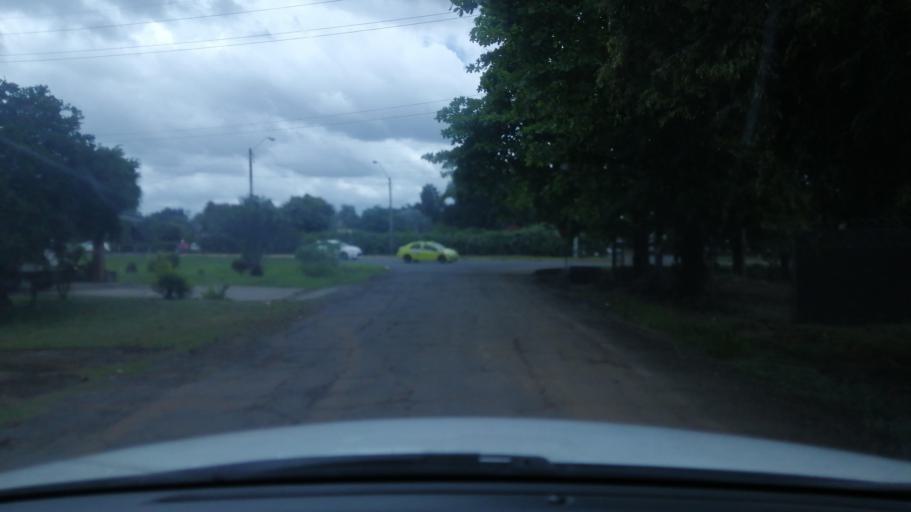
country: PA
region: Chiriqui
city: David
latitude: 8.4446
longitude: -82.4298
